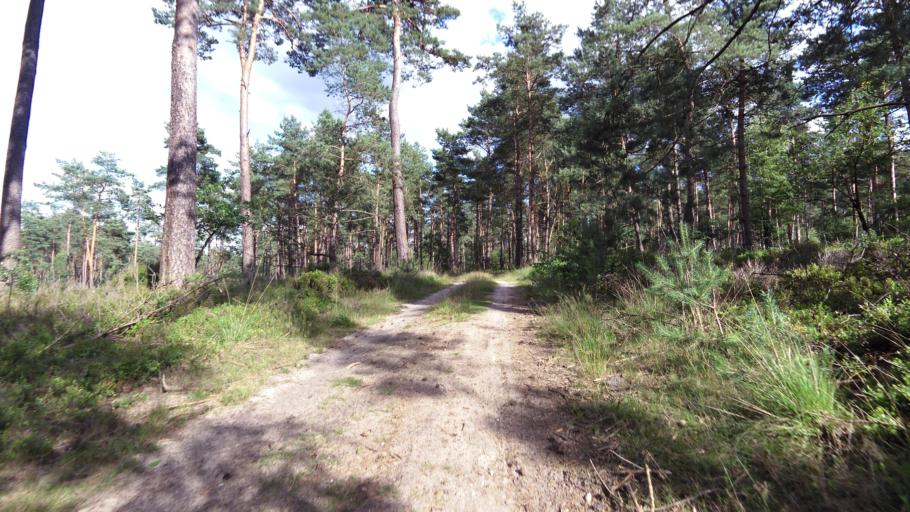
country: NL
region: Gelderland
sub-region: Gemeente Apeldoorn
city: Uddel
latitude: 52.2856
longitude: 5.8566
